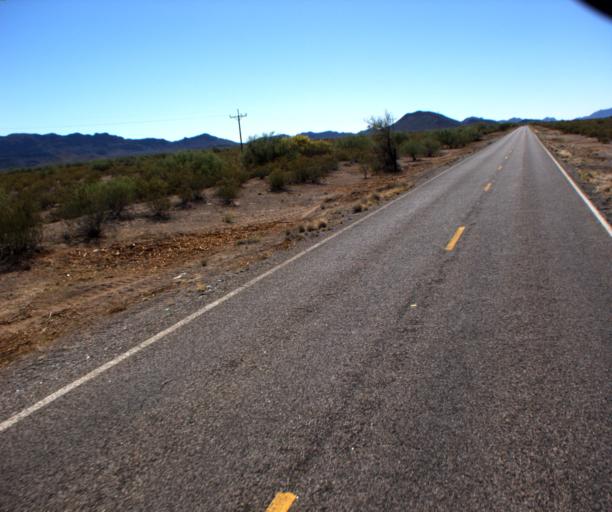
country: US
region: Arizona
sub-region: Pima County
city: Ajo
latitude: 32.3124
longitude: -112.7646
